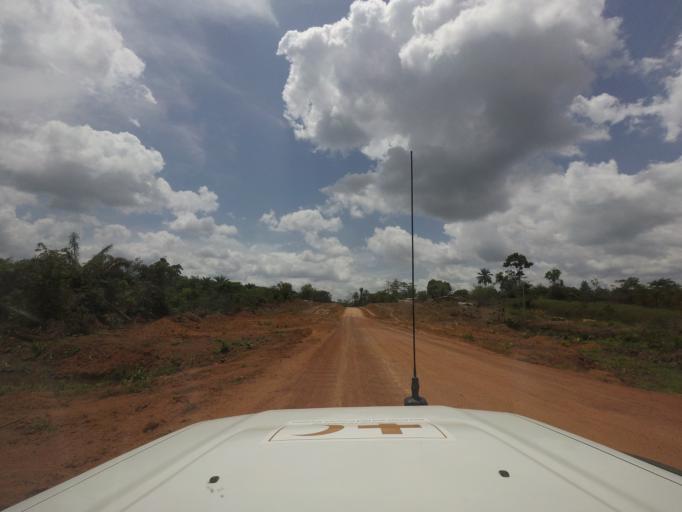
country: LR
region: Nimba
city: Sanniquellie
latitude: 7.2293
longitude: -8.9176
